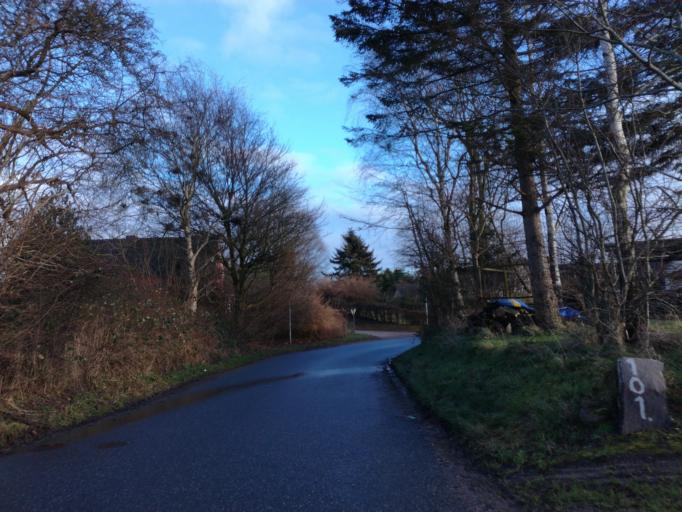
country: DK
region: South Denmark
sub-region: Fredericia Kommune
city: Taulov
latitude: 55.5595
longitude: 9.6033
